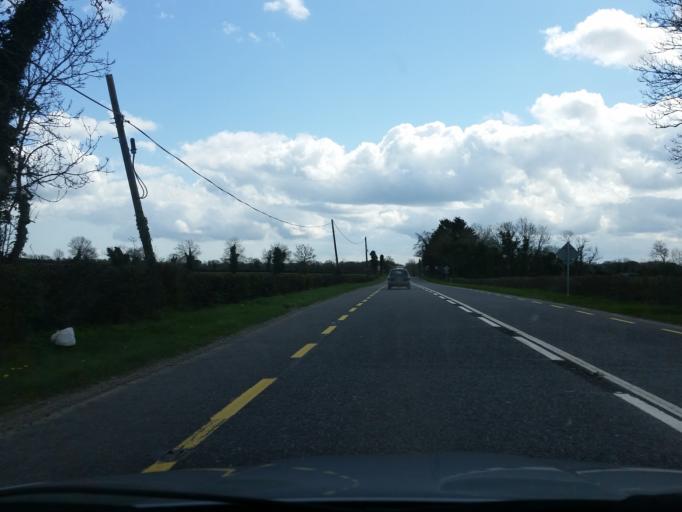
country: IE
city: Kentstown
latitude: 53.6476
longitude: -6.5101
